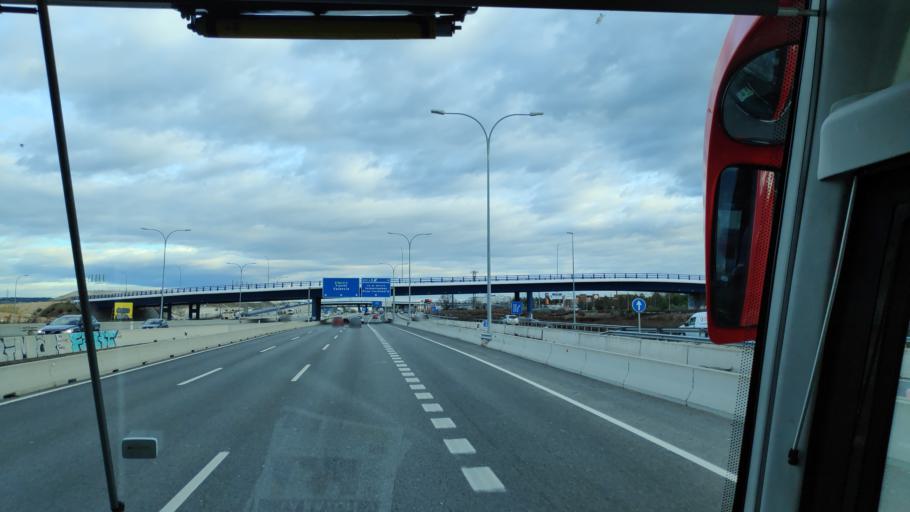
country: ES
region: Madrid
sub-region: Provincia de Madrid
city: Villa de Vallecas
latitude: 40.3706
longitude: -3.5911
